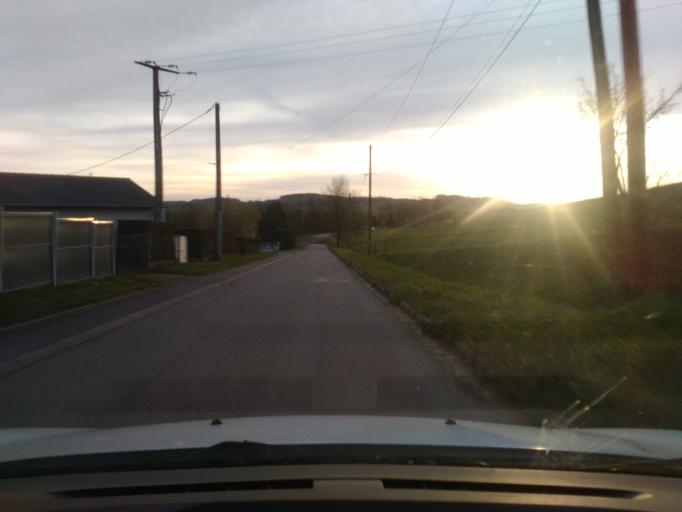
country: FR
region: Lorraine
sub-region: Departement des Vosges
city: Charmes
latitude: 48.3626
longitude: 6.2551
